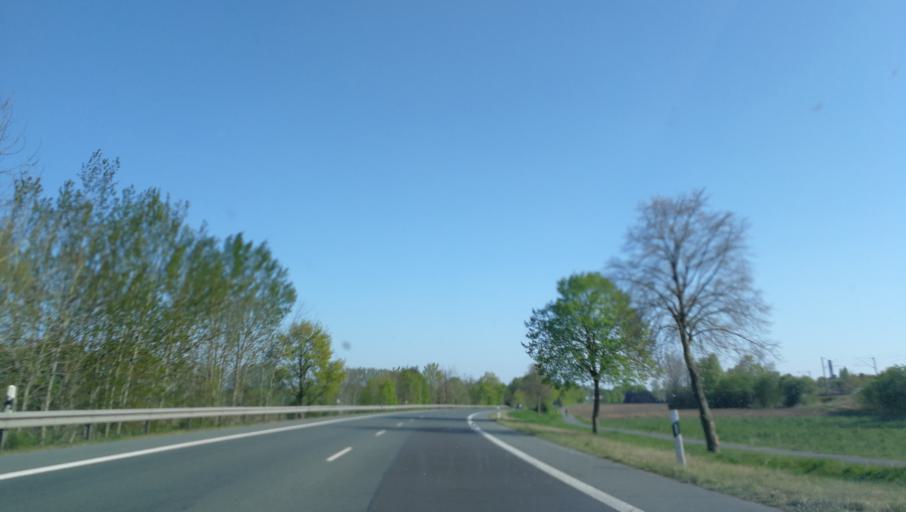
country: DE
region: North Rhine-Westphalia
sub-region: Regierungsbezirk Munster
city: Rheine
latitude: 52.2555
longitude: 7.4580
